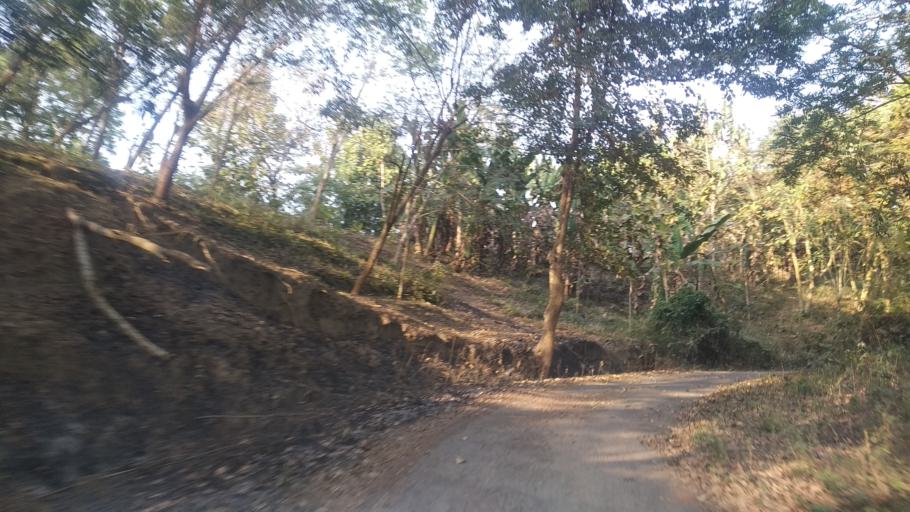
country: IN
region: Tripura
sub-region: West Tripura
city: Sonamura
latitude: 23.4441
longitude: 91.3646
